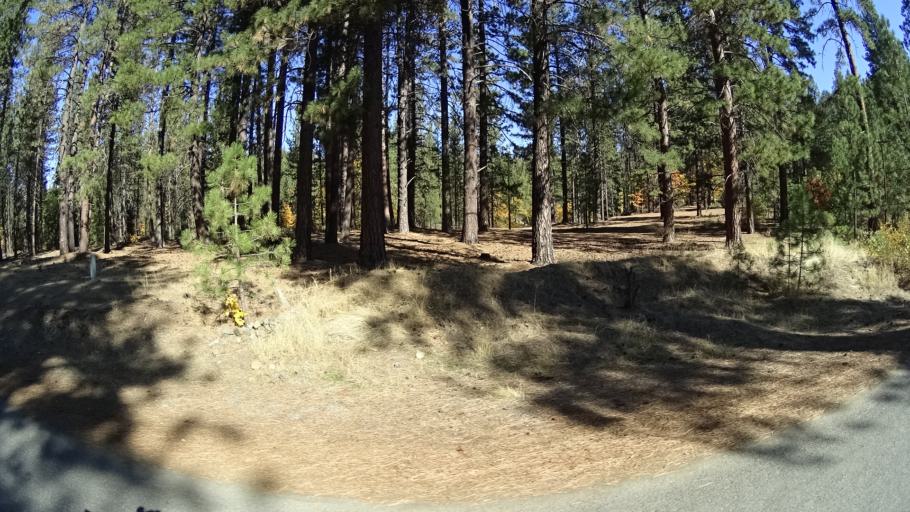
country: US
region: California
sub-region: Siskiyou County
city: Yreka
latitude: 41.5898
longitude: -122.9572
